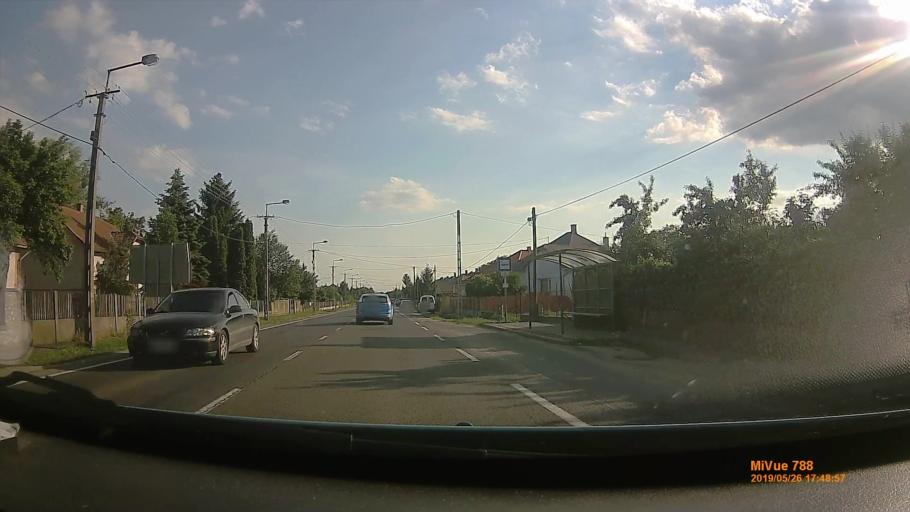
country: HU
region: Borsod-Abauj-Zemplen
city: Szikszo
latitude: 48.1924
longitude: 20.9275
